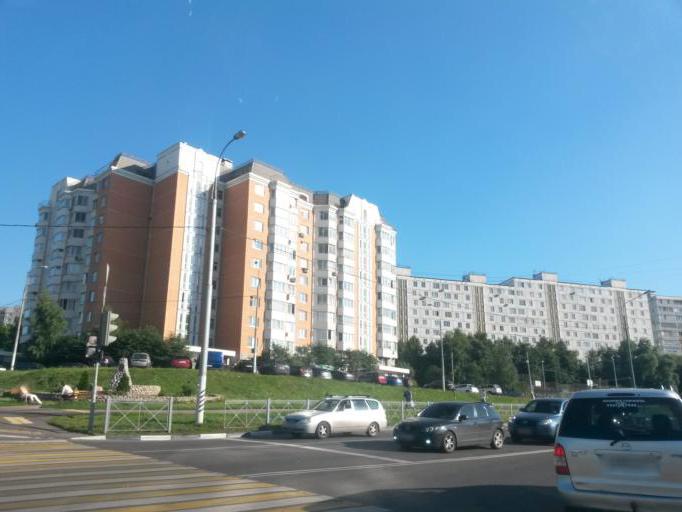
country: RU
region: Moscow
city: Zyablikovo
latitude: 55.6245
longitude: 37.7537
